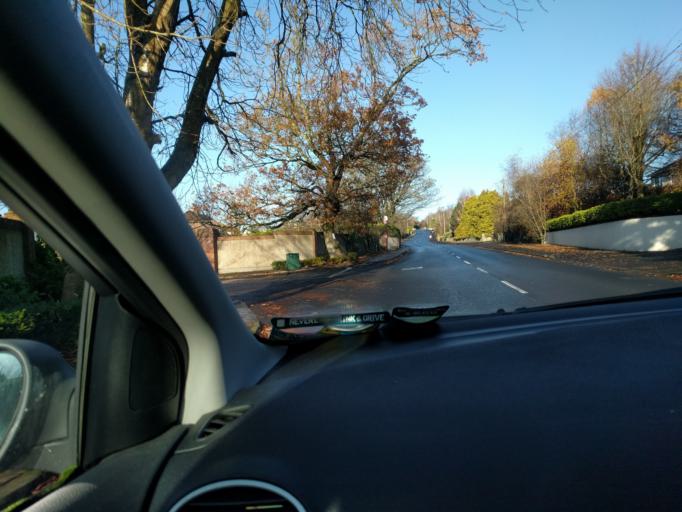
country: IE
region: Munster
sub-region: County Limerick
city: Annacotty
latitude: 52.6540
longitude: -8.5647
